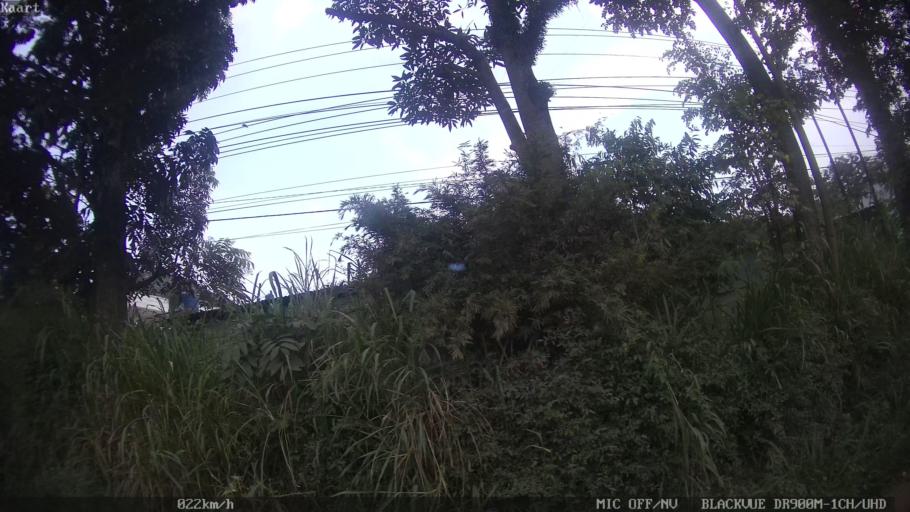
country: ID
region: Lampung
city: Panjang
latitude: -5.4189
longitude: 105.3346
